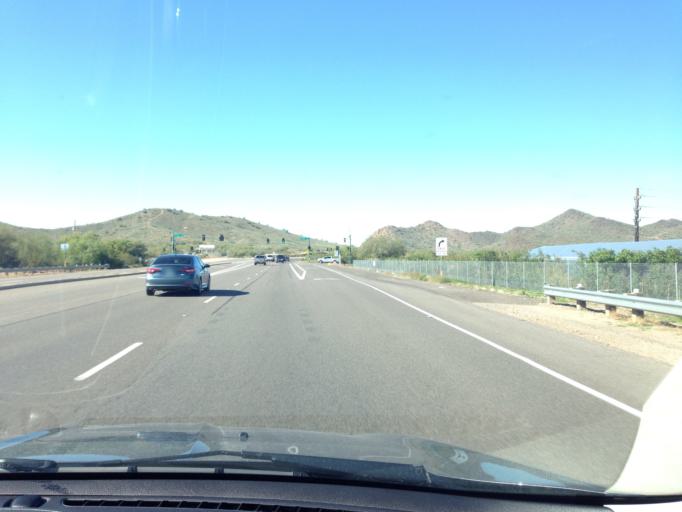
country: US
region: Arizona
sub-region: Maricopa County
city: Anthem
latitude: 33.7992
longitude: -112.0809
